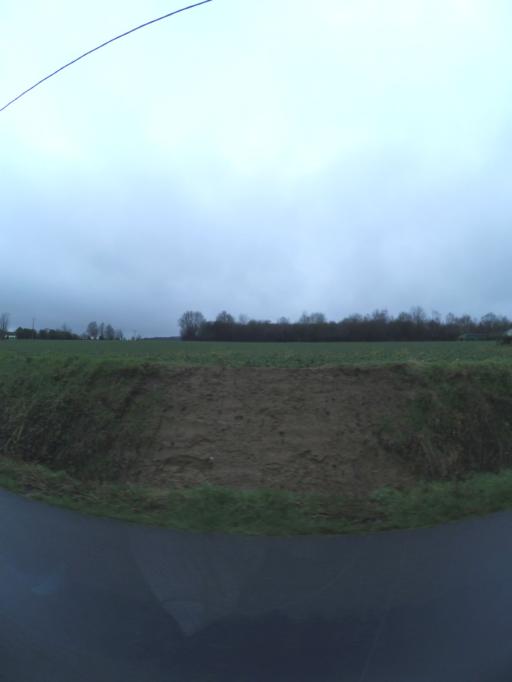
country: FR
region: Pays de la Loire
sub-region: Departement de la Sarthe
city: Saint-Saturnin
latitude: 48.0564
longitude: 0.1574
